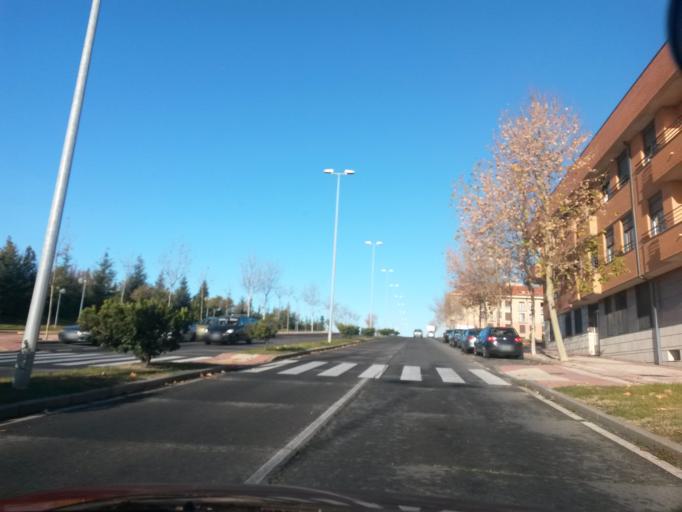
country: ES
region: Castille and Leon
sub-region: Provincia de Salamanca
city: Salamanca
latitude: 40.9742
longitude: -5.6816
